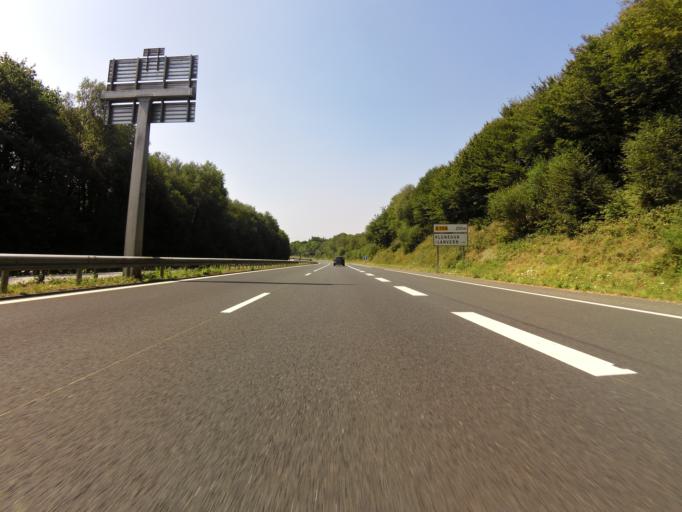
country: FR
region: Brittany
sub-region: Departement du Finistere
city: Pluguffan
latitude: 47.9556
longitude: -4.1733
